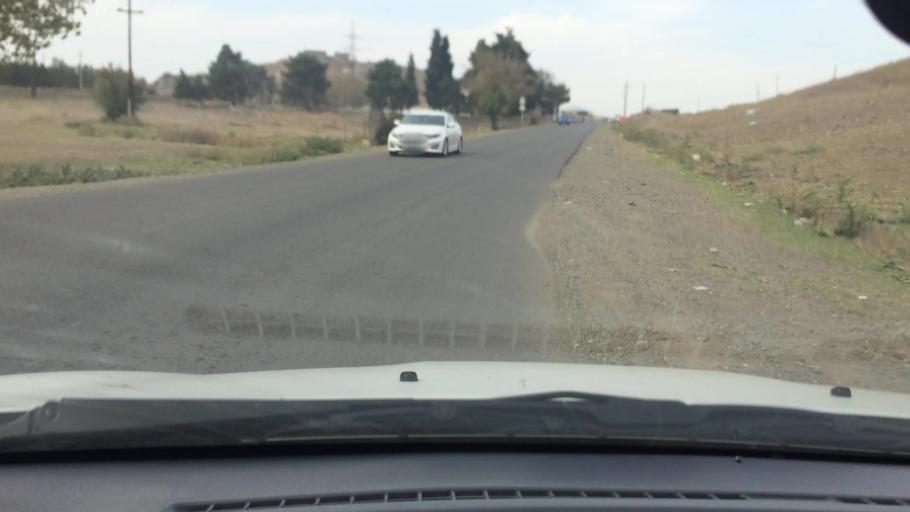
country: GE
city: Naghvarevi
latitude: 41.3608
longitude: 44.8371
